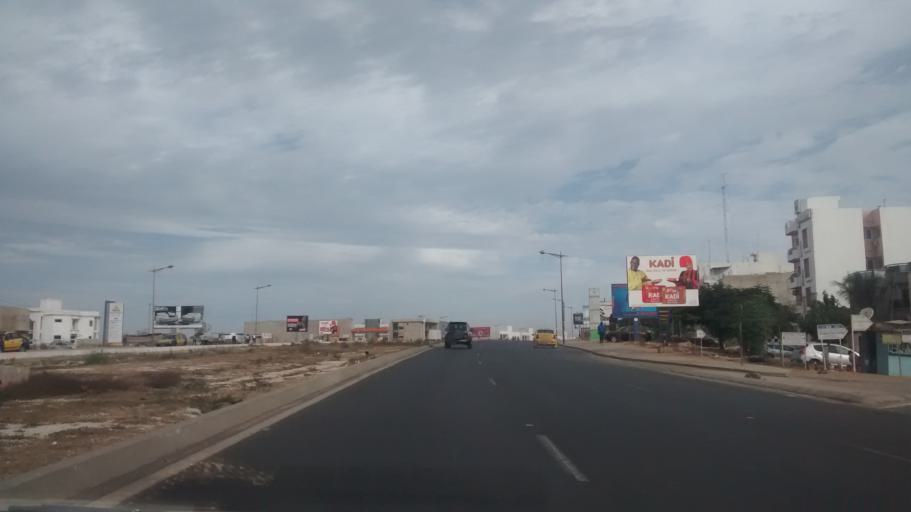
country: SN
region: Dakar
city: Mermoz Boabab
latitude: 14.7310
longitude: -17.4729
